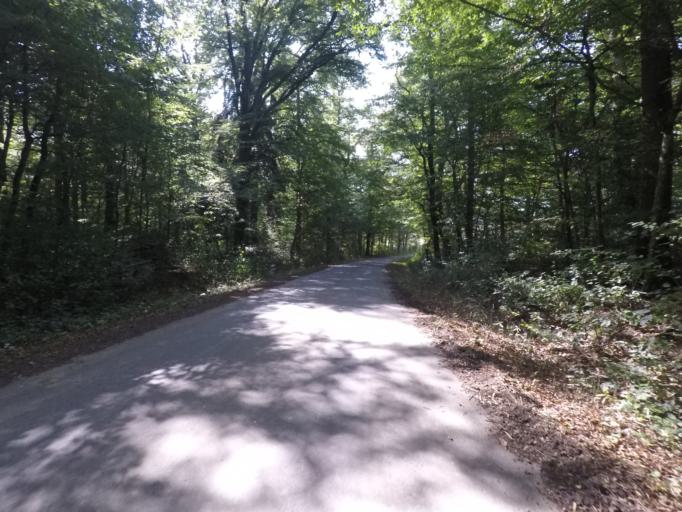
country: LU
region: Luxembourg
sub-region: Canton de Capellen
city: Kehlen
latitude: 49.6507
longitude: 6.0221
